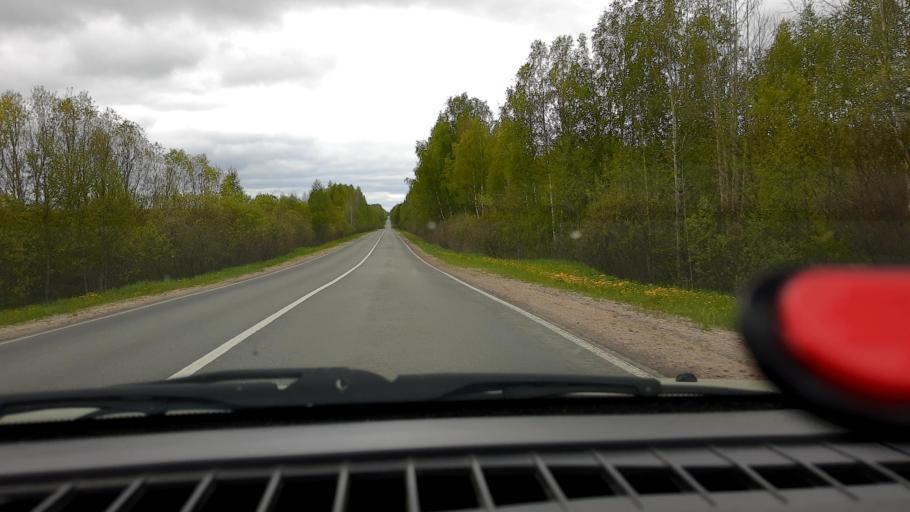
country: RU
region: Nizjnij Novgorod
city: Uren'
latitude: 57.2739
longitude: 45.6302
